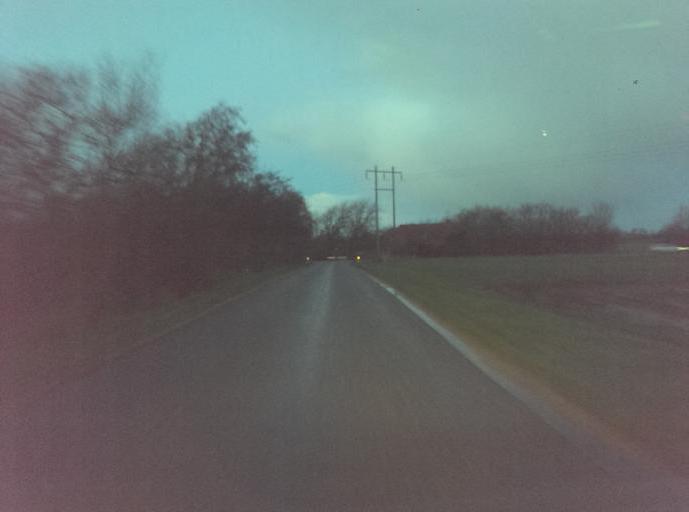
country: DK
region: South Denmark
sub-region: Esbjerg Kommune
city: Bramming
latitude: 55.4568
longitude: 8.6588
